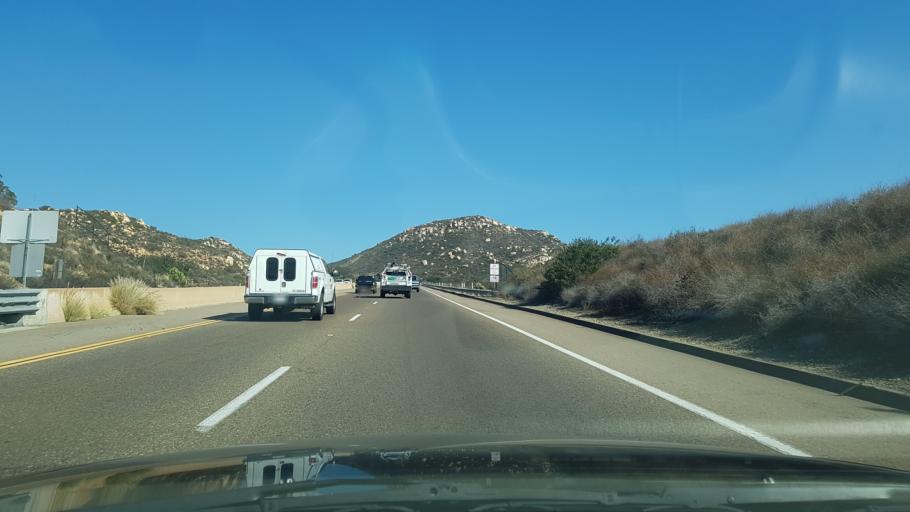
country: US
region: California
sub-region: San Diego County
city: Poway
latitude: 32.9512
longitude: -116.9825
